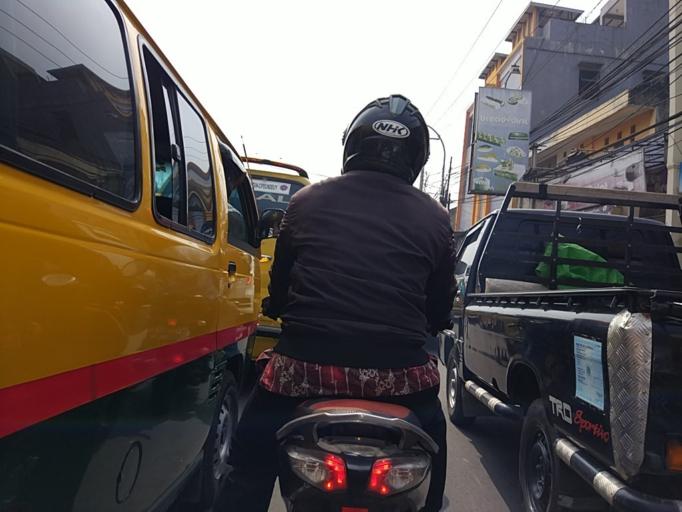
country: ID
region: West Java
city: Padalarang
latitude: -6.8417
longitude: 107.4856
